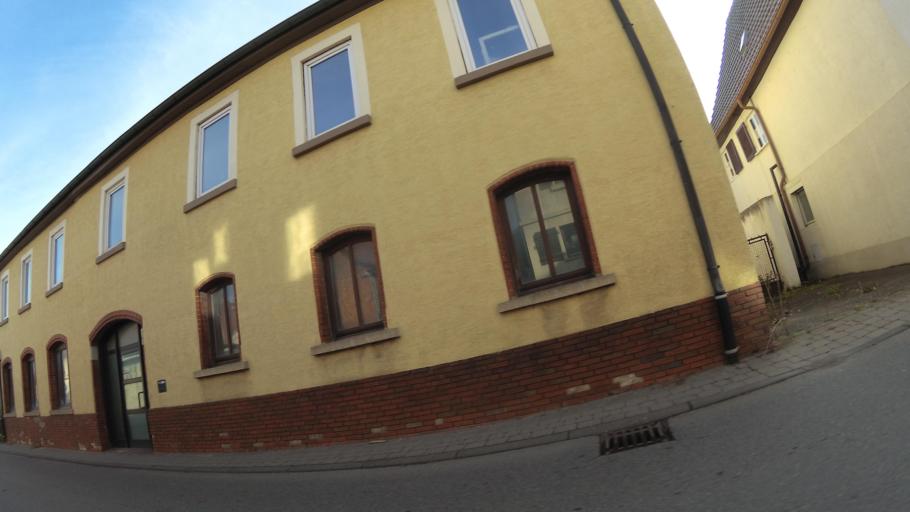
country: DE
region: Baden-Wuerttemberg
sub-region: Regierungsbezirk Stuttgart
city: Offenau
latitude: 49.2503
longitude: 9.1961
